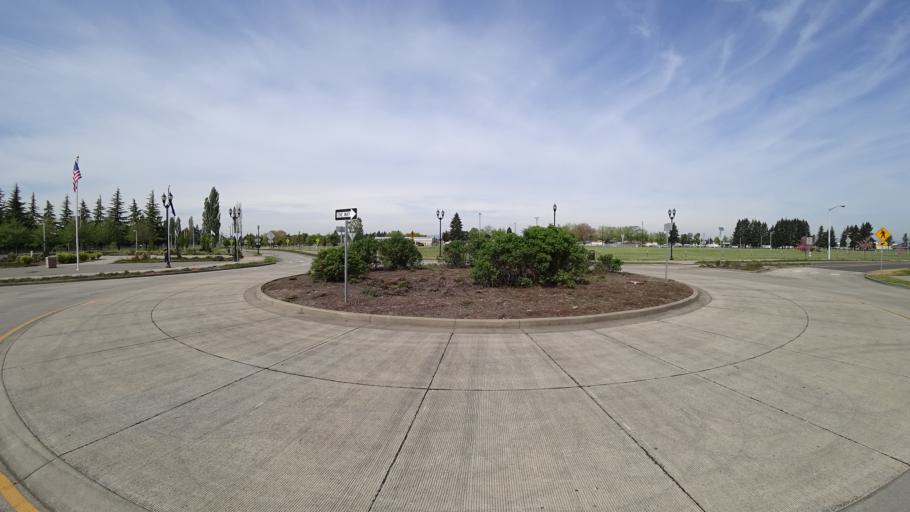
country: US
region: Oregon
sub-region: Washington County
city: Hillsboro
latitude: 45.5286
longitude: -122.9465
